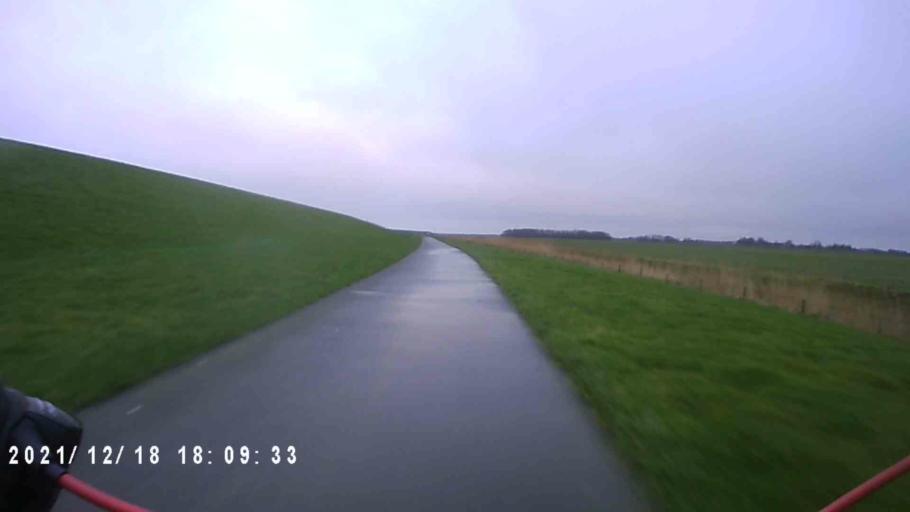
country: NL
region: Friesland
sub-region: Gemeente Dongeradeel
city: Ternaard
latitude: 53.3869
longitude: 5.9311
